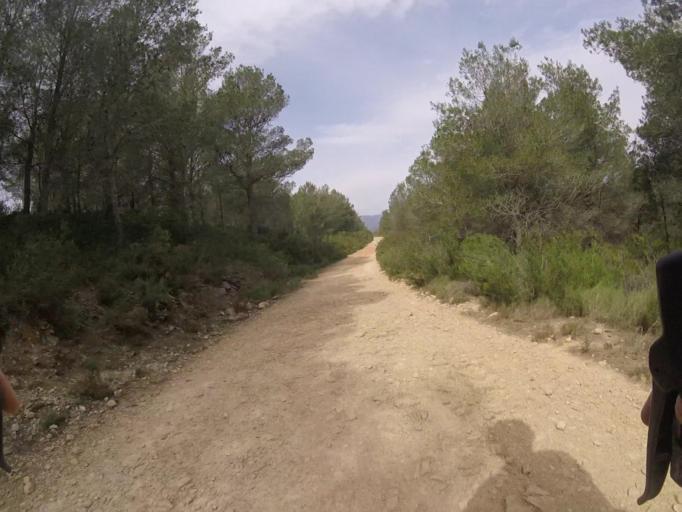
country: ES
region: Valencia
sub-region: Provincia de Castello
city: Cuevas de Vinroma
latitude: 40.2588
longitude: 0.1066
